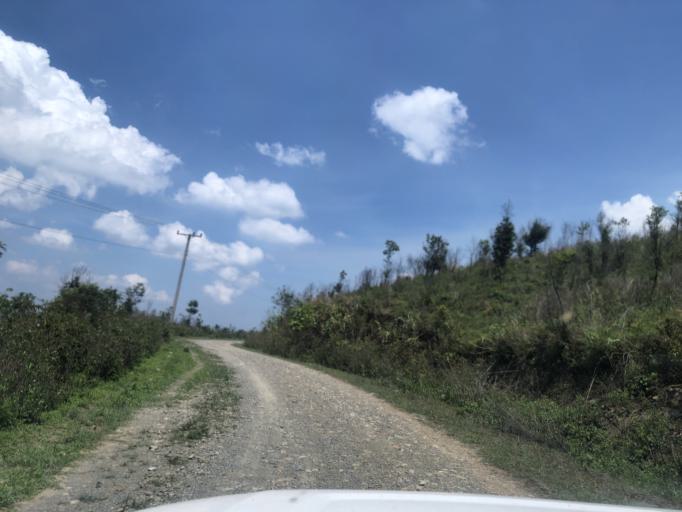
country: LA
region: Phongsali
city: Phongsali
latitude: 21.4212
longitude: 102.1822
